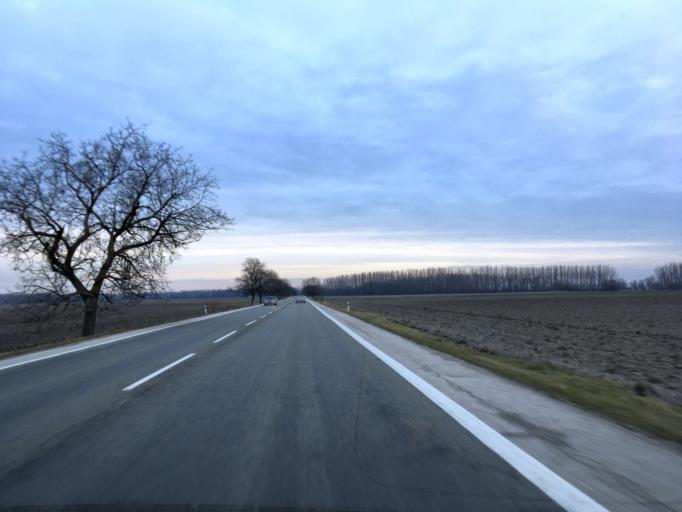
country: SK
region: Trnavsky
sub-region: Okres Dunajska Streda
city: Velky Meder
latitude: 47.9140
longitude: 17.7299
